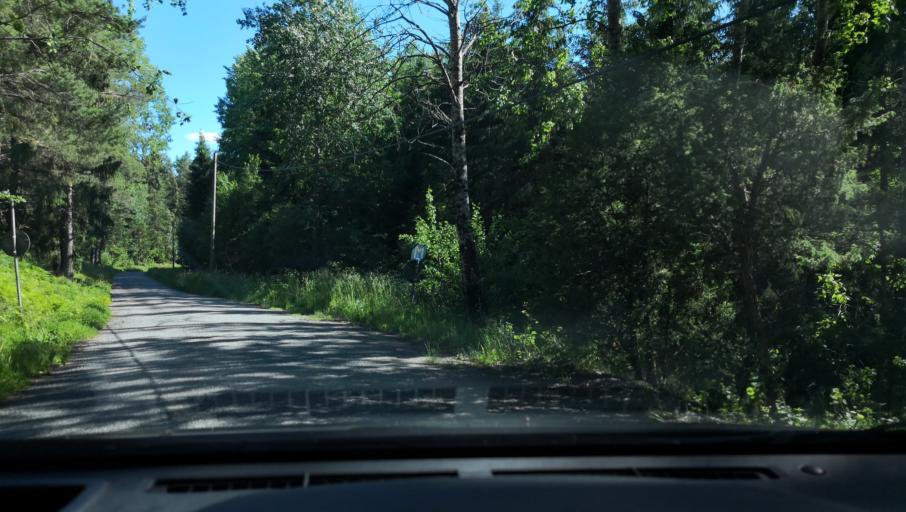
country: SE
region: Soedermanland
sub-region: Eskilstuna Kommun
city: Arla
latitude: 59.3262
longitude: 16.5962
